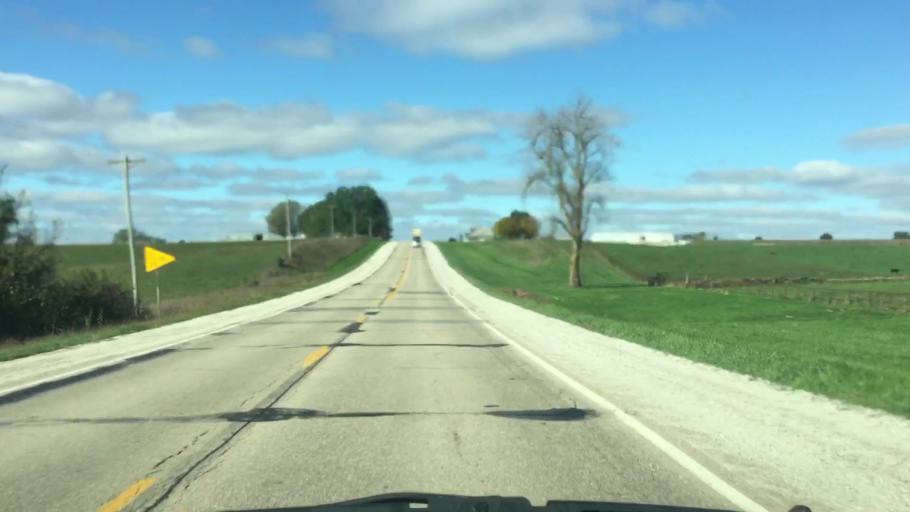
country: US
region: Iowa
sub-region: Decatur County
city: Leon
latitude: 40.7419
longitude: -93.8105
